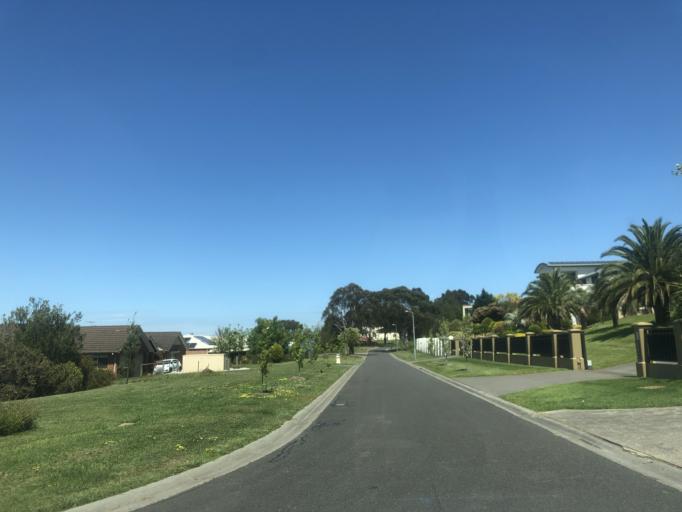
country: AU
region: Victoria
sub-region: Casey
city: Narre Warren North
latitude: -37.9811
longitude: 145.2884
